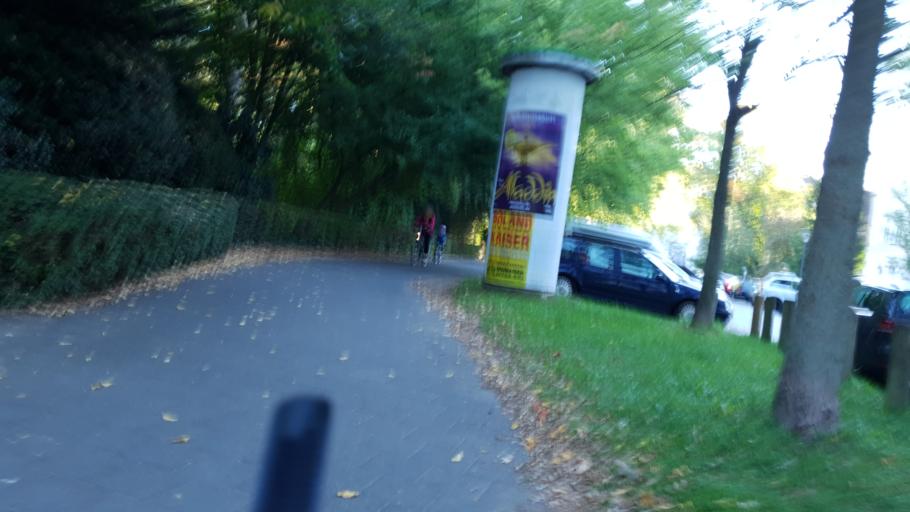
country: DE
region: Schleswig-Holstein
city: Kiel
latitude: 54.3259
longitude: 10.1241
